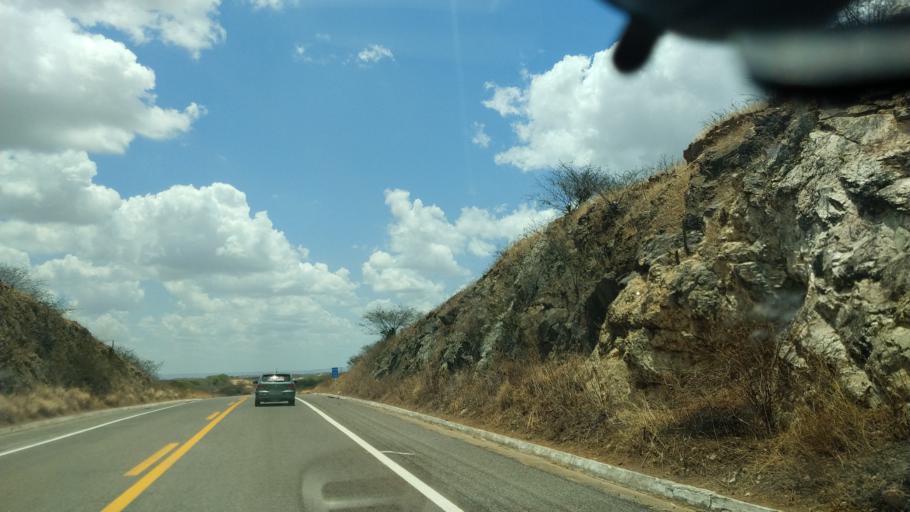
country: BR
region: Rio Grande do Norte
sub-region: Cerro Cora
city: Cerro Cora
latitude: -6.2100
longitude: -36.3065
